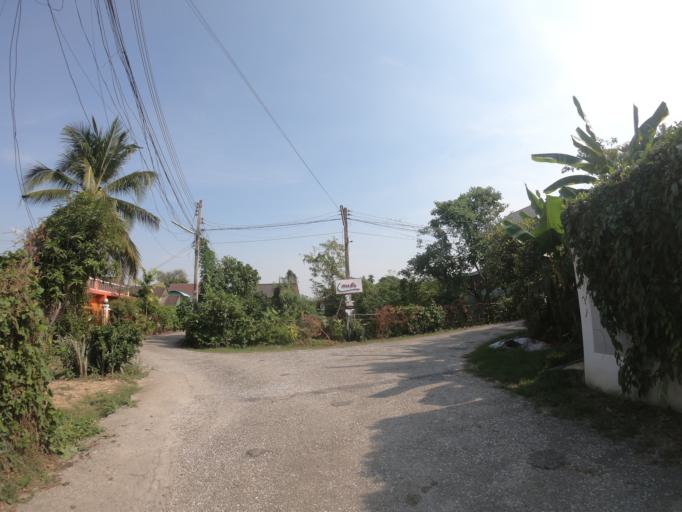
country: TH
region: Chiang Mai
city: Chiang Mai
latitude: 18.7697
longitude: 99.0152
